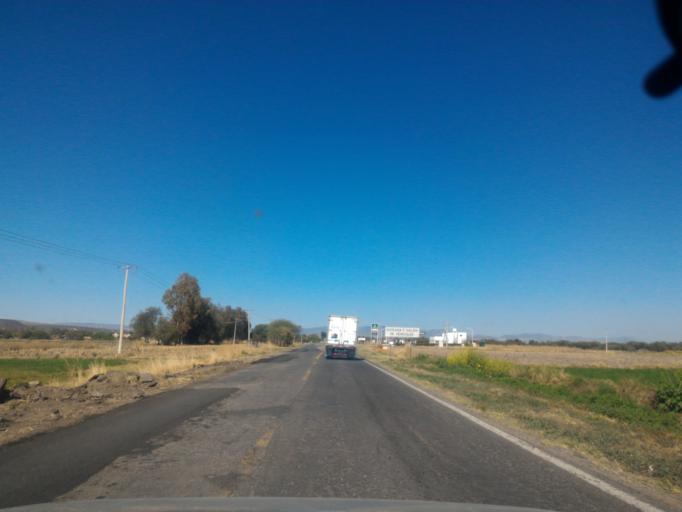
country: MX
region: Guanajuato
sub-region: San Francisco del Rincon
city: San Roque de Montes
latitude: 21.0245
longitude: -101.7858
